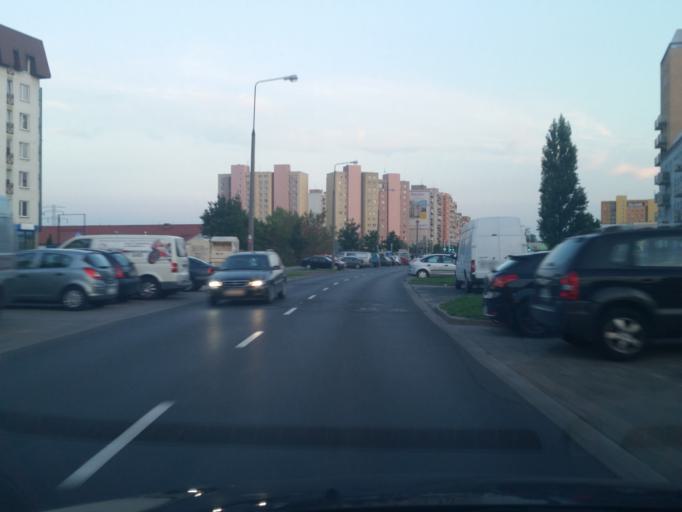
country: PL
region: Masovian Voivodeship
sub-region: Warszawa
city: Bialoleka
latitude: 52.3187
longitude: 20.9587
